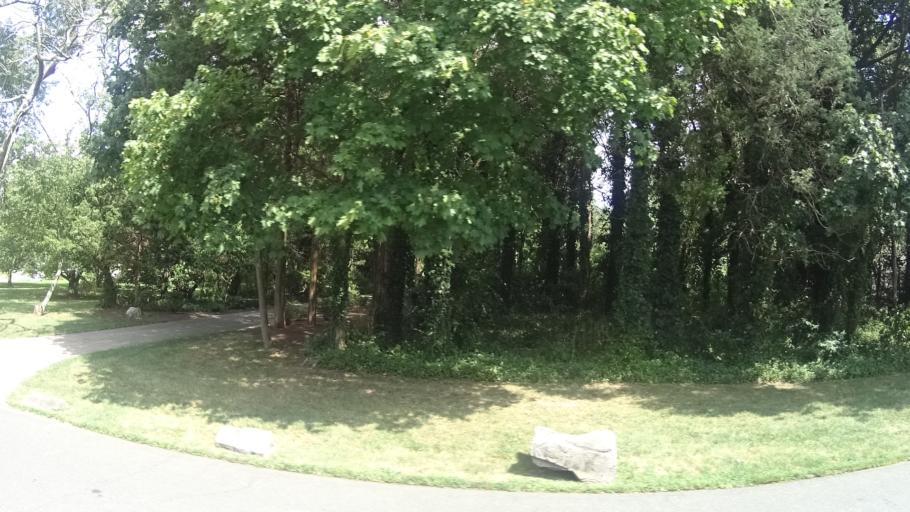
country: US
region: New Jersey
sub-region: Monmouth County
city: Brielle
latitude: 40.1133
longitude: -74.0891
